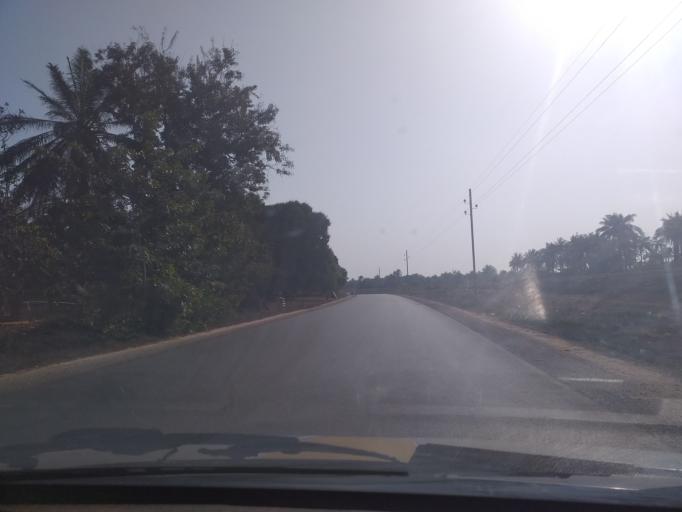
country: GN
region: Boke
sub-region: Boke Prefecture
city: Sangueya
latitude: 10.7783
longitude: -14.4289
